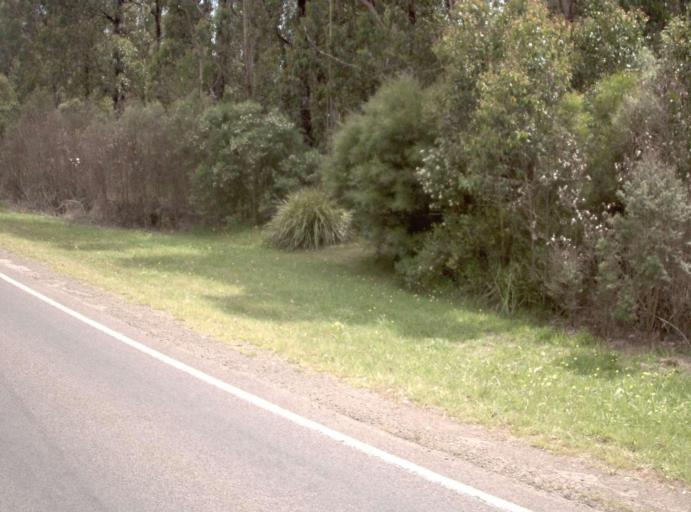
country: AU
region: Victoria
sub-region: Latrobe
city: Moe
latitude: -37.9271
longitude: 146.4013
